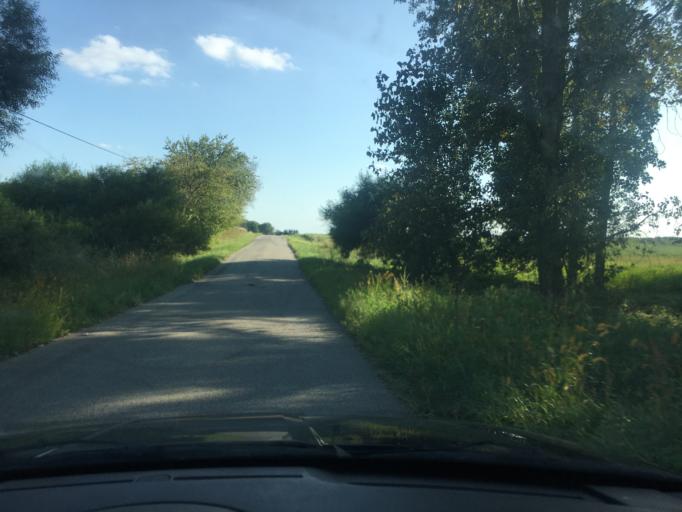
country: US
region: Ohio
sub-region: Logan County
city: West Liberty
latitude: 40.2442
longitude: -83.7855
